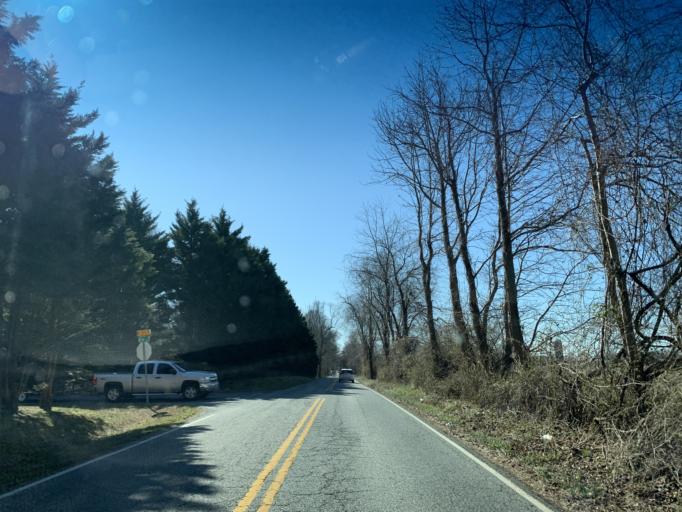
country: US
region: Maryland
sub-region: Cecil County
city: Charlestown
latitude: 39.4585
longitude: -75.8924
